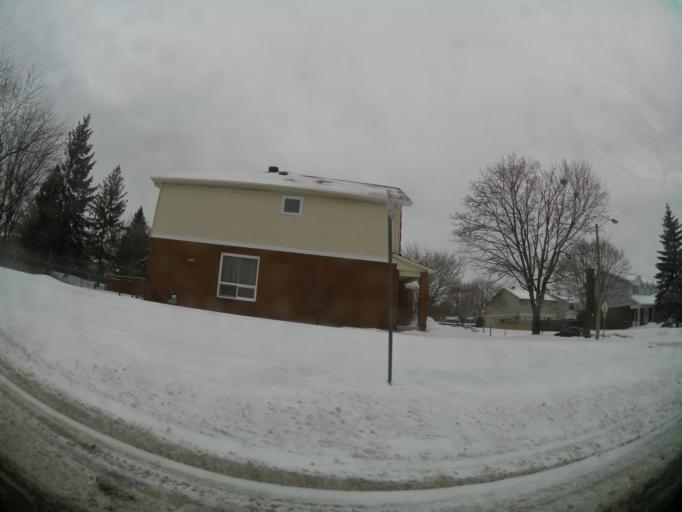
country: CA
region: Ontario
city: Ottawa
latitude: 45.3727
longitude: -75.6151
